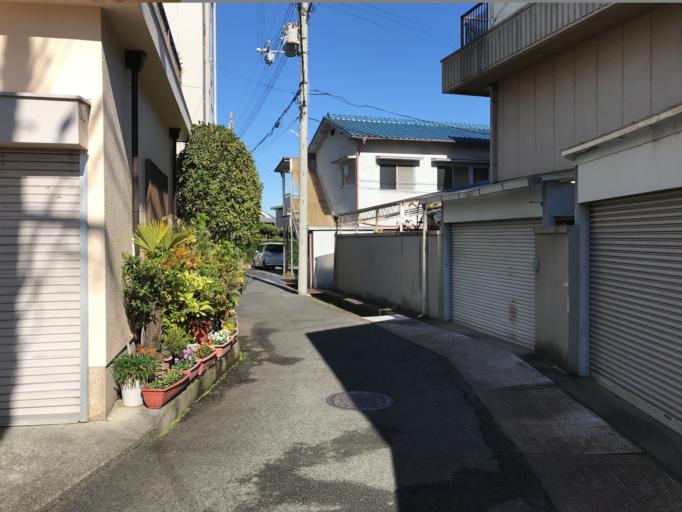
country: JP
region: Osaka
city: Tondabayashicho
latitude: 34.4584
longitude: 135.5767
